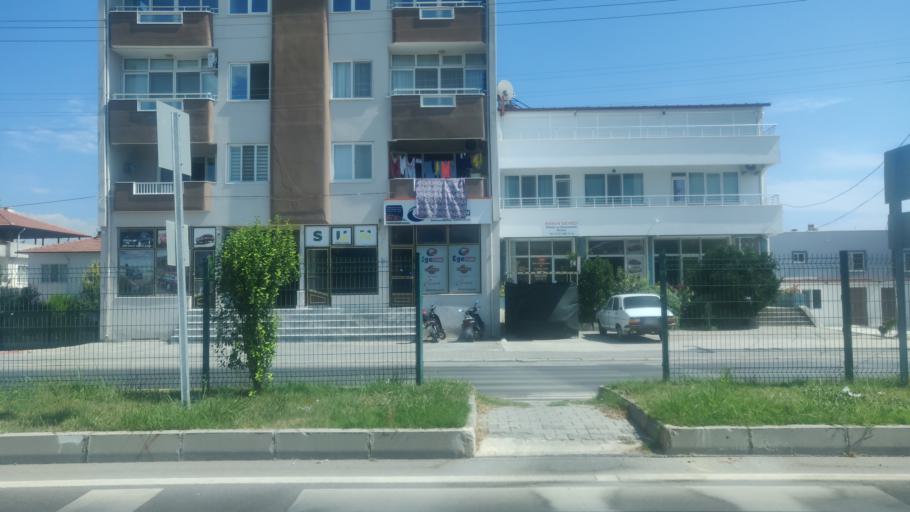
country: TR
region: Mugla
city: Dalaman
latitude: 36.7767
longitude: 28.8015
